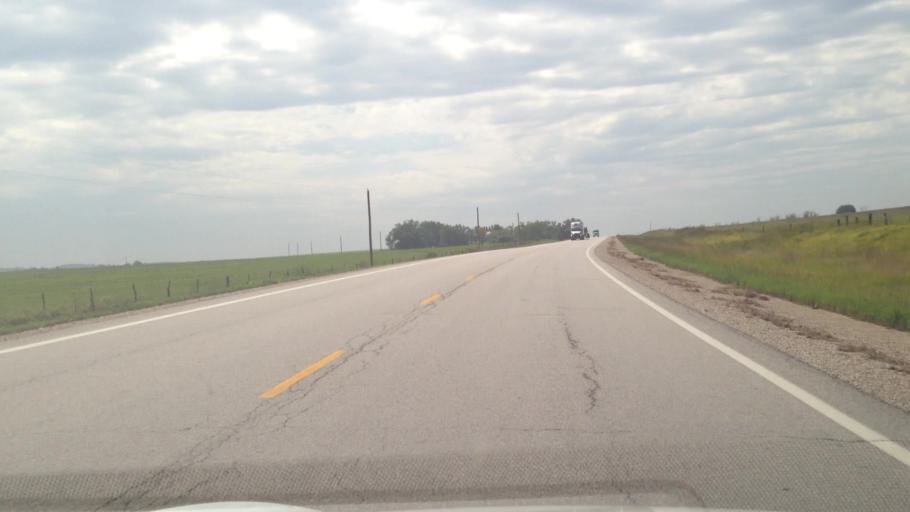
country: US
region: Kansas
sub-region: Anderson County
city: Garnett
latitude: 38.1890
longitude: -95.2412
